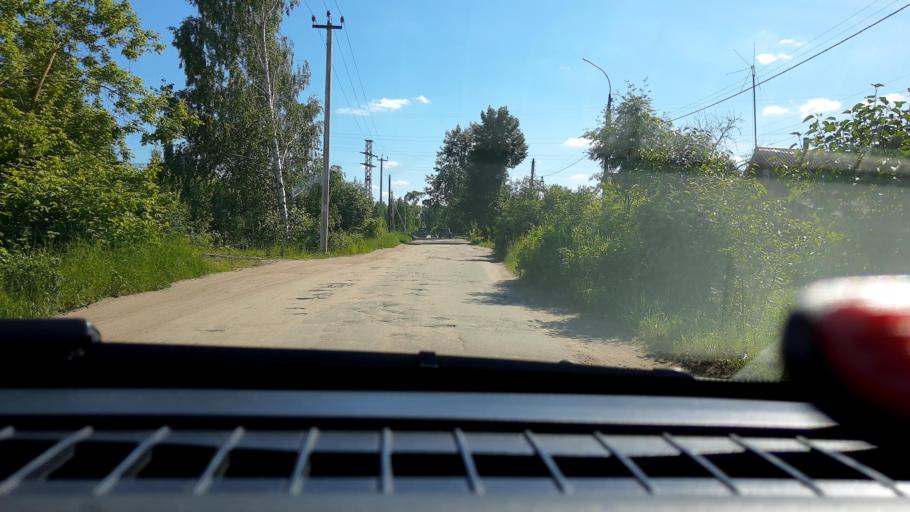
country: RU
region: Nizjnij Novgorod
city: Gidrotorf
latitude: 56.5181
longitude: 43.5397
